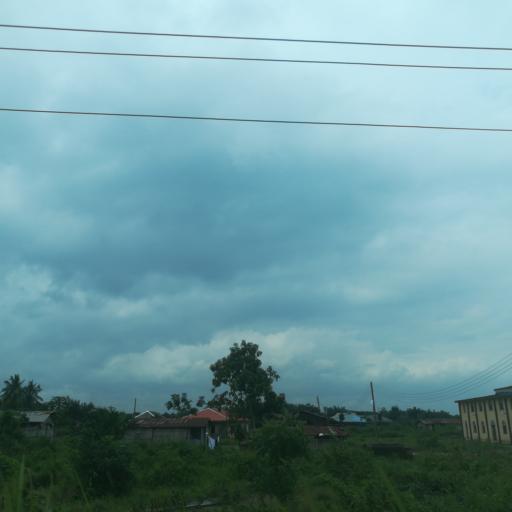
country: NG
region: Lagos
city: Ejirin
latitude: 6.6557
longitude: 3.7997
